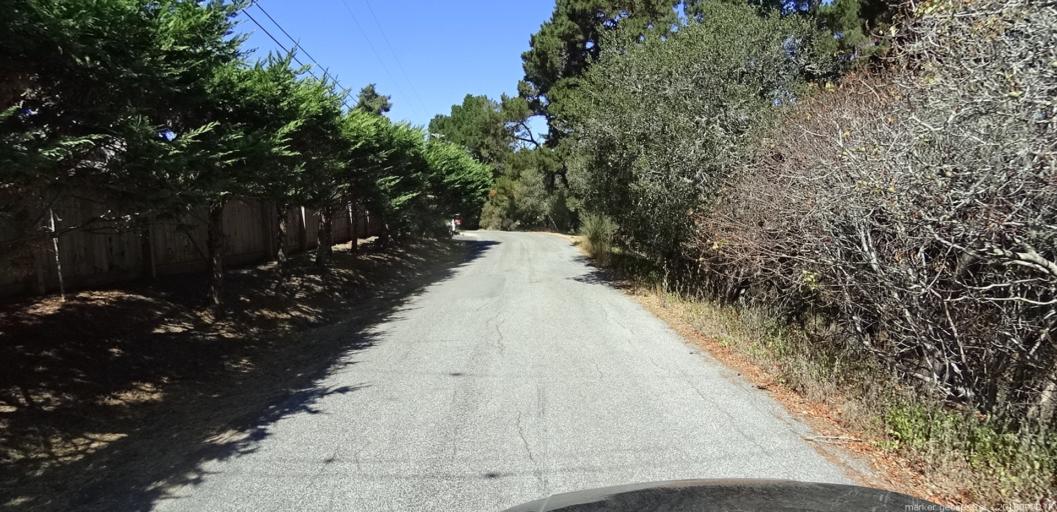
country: US
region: California
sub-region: Monterey County
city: Del Rey Oaks
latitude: 36.5785
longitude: -121.8652
